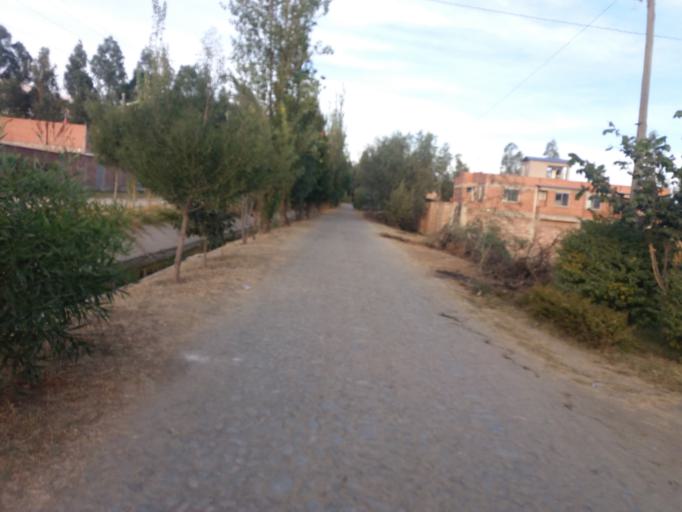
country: BO
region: Cochabamba
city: Cochabamba
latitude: -17.3567
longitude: -66.1996
